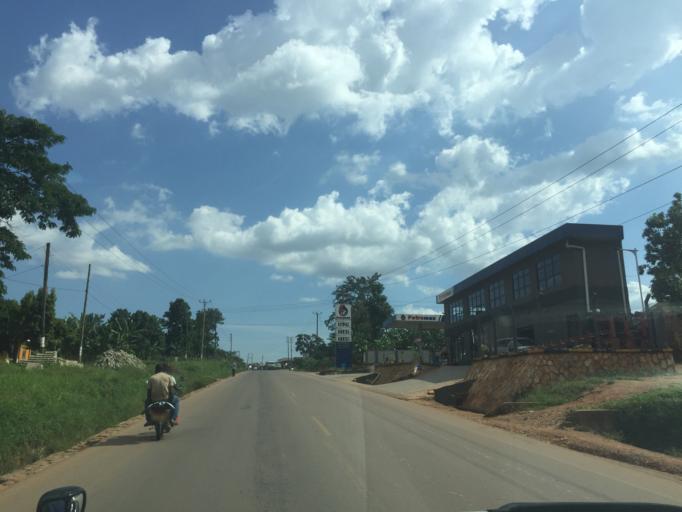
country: UG
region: Central Region
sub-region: Wakiso District
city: Wakiso
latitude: 0.4704
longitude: 32.5187
